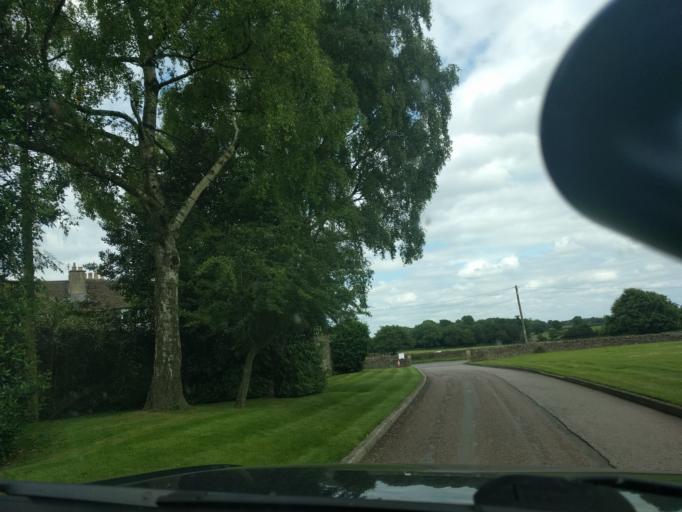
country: GB
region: England
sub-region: Wiltshire
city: Biddestone
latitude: 51.4484
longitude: -2.2001
